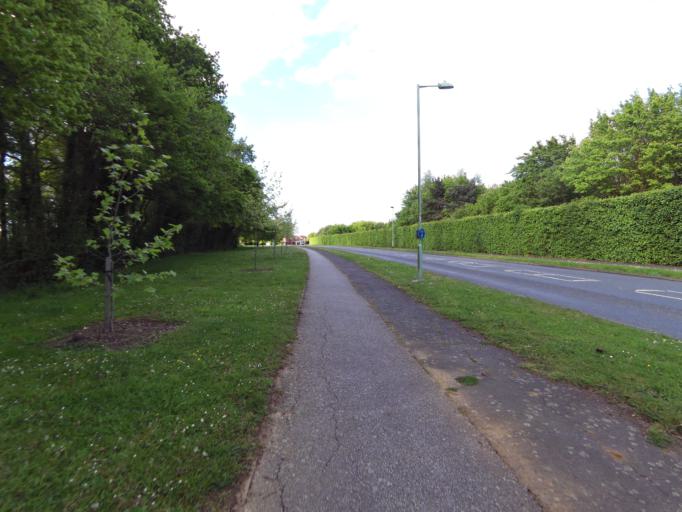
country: GB
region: England
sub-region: Suffolk
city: Stowmarket
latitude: 52.1933
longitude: 0.9753
